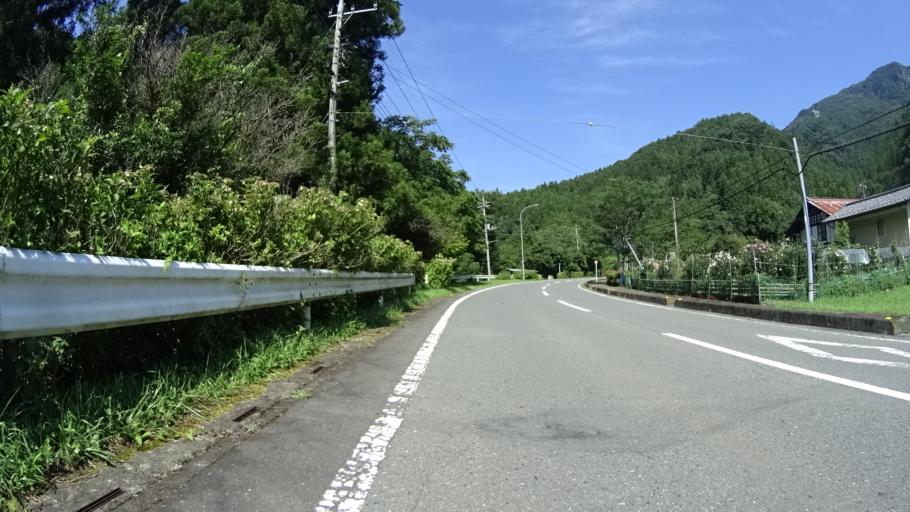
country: JP
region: Saitama
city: Chichibu
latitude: 36.0367
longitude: 138.9155
